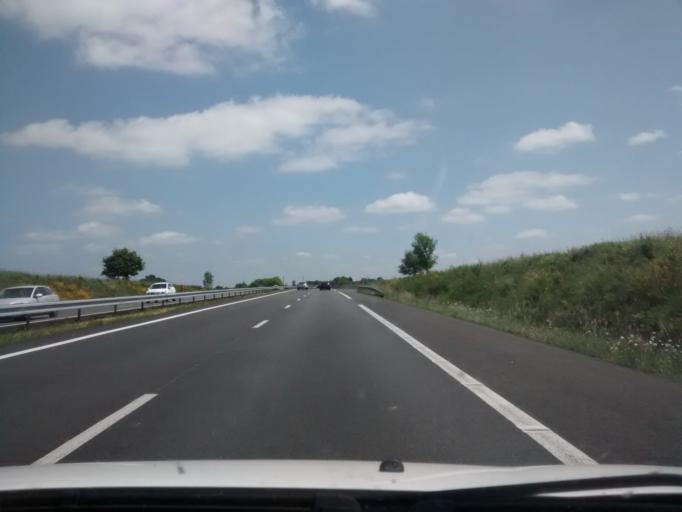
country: FR
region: Pays de la Loire
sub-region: Departement de la Mayenne
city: Sainte-Suzanne
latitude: 48.0375
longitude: -0.3735
